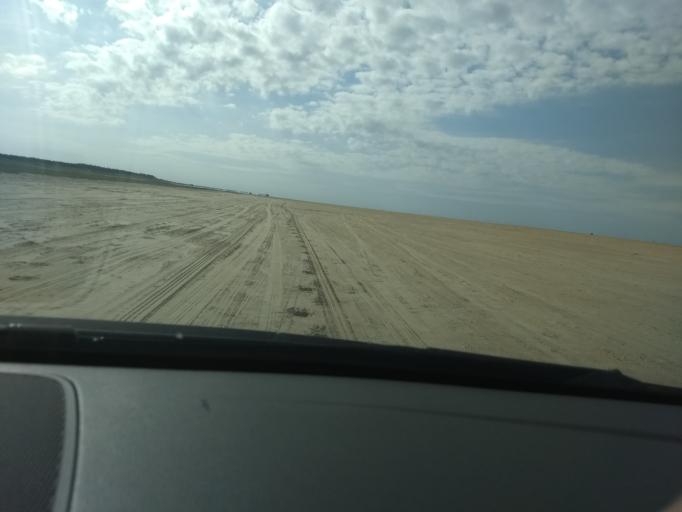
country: DE
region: Schleswig-Holstein
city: List
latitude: 55.0893
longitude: 8.5017
